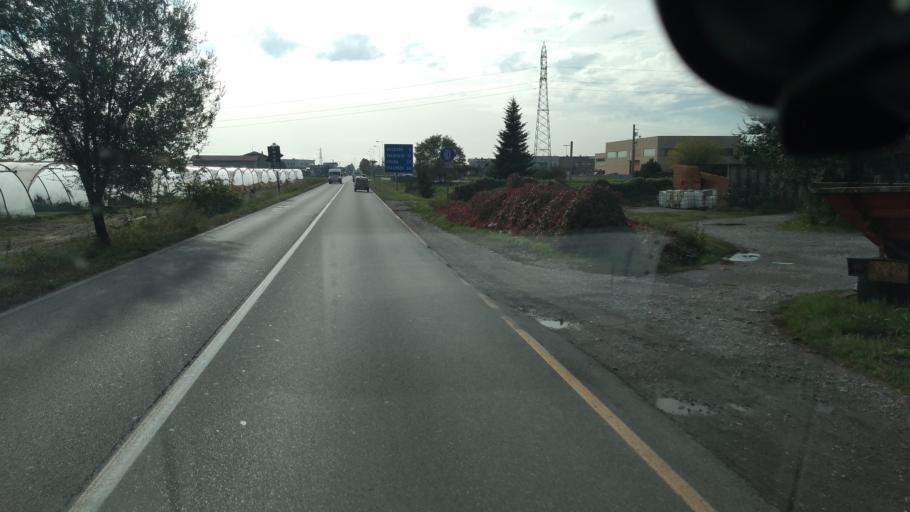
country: IT
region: Lombardy
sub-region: Provincia di Bergamo
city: Zanica
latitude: 45.6261
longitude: 9.6890
